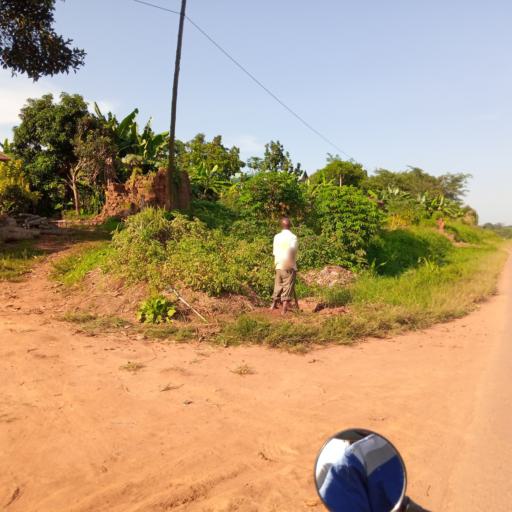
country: UG
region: Central Region
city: Masaka
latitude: -0.4290
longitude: 31.6661
